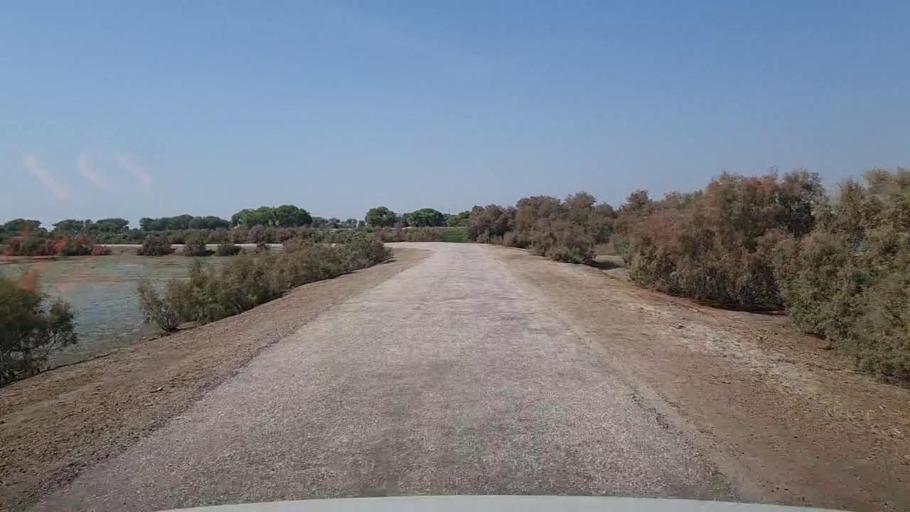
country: PK
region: Sindh
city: Kandhkot
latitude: 28.3375
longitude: 69.3639
